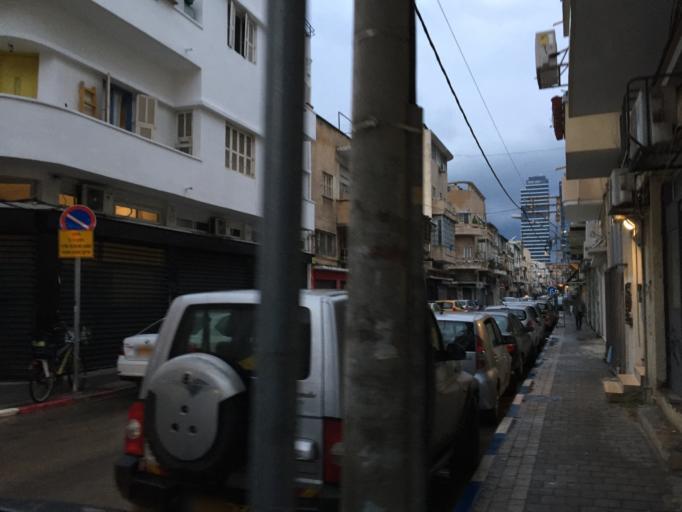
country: IL
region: Tel Aviv
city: Yafo
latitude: 32.0574
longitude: 34.7700
